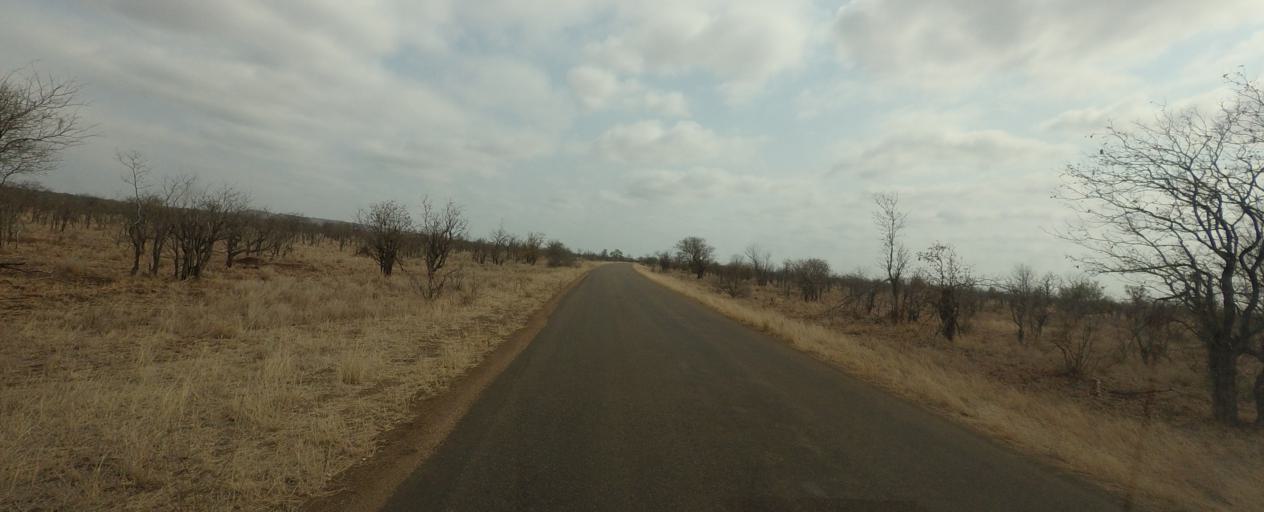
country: ZA
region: Limpopo
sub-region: Vhembe District Municipality
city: Mutale
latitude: -22.6151
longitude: 31.1740
